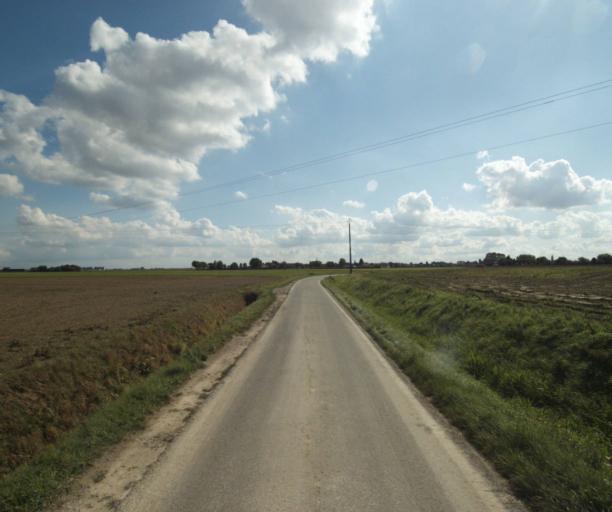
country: FR
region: Nord-Pas-de-Calais
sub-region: Departement du Nord
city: La Bassee
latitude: 50.5500
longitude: 2.8076
